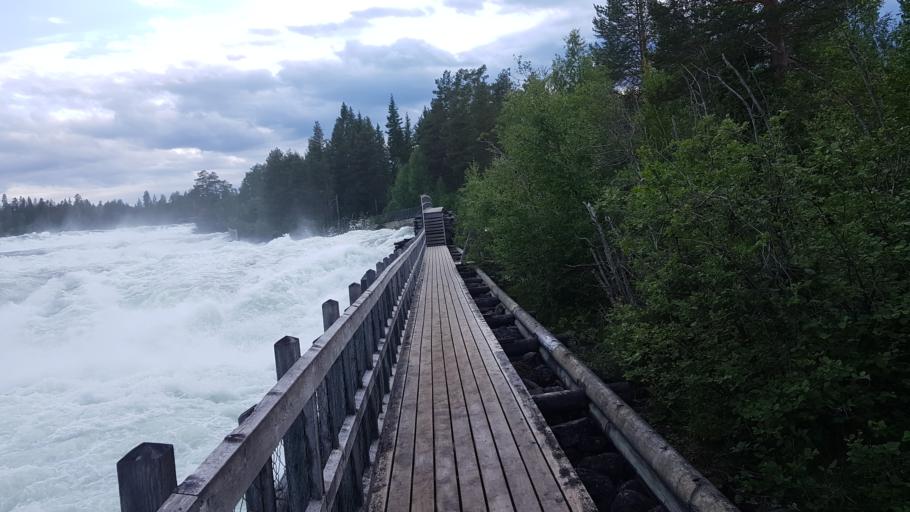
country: SE
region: Norrbotten
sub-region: Alvsbyns Kommun
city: AElvsbyn
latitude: 65.8529
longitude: 20.4116
